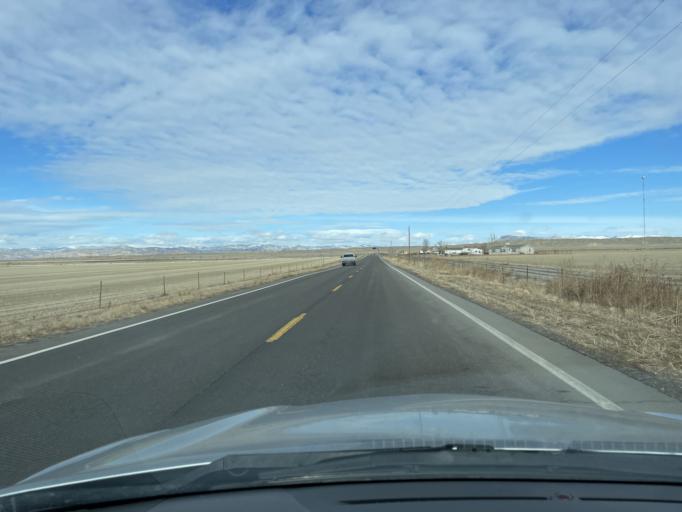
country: US
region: Colorado
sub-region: Mesa County
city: Loma
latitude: 39.2590
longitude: -108.8128
